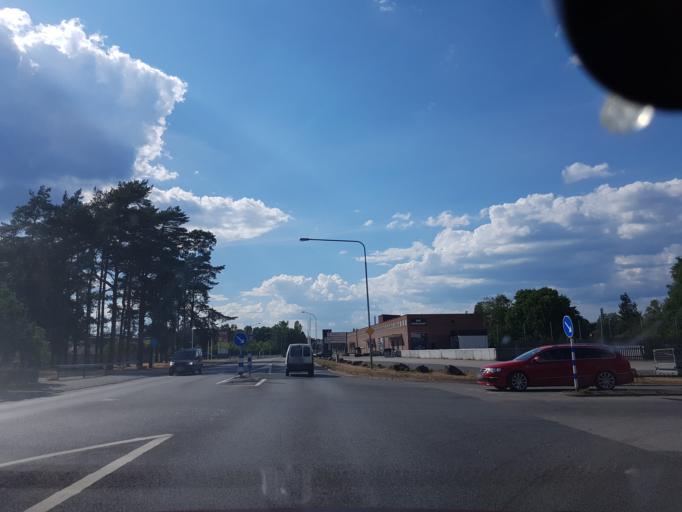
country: SE
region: Joenkoeping
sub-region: Gislaveds Kommun
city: Gislaved
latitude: 57.2986
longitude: 13.5564
